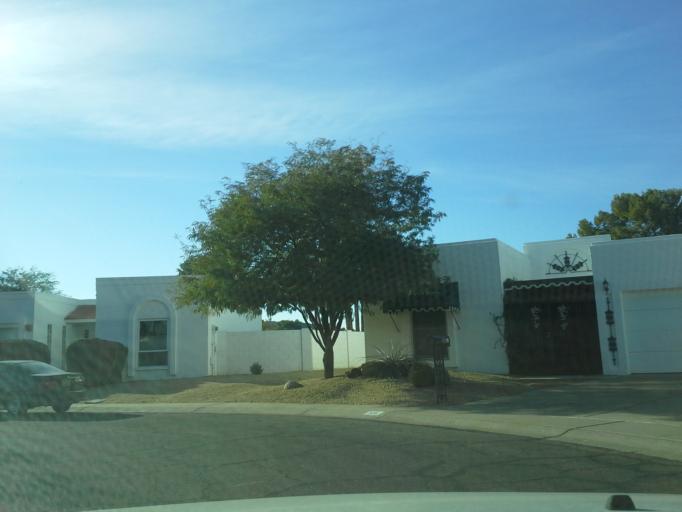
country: US
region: Arizona
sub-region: Maricopa County
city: Glendale
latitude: 33.6136
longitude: -112.0692
